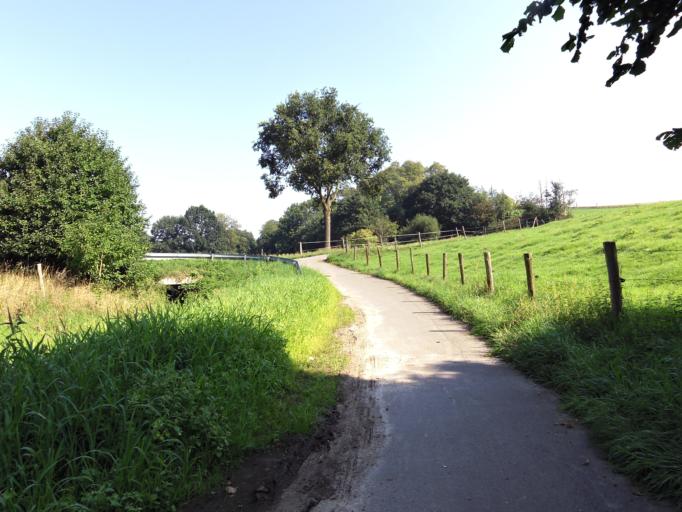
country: DE
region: North Rhine-Westphalia
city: Geilenkirchen
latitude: 50.9894
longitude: 6.1857
